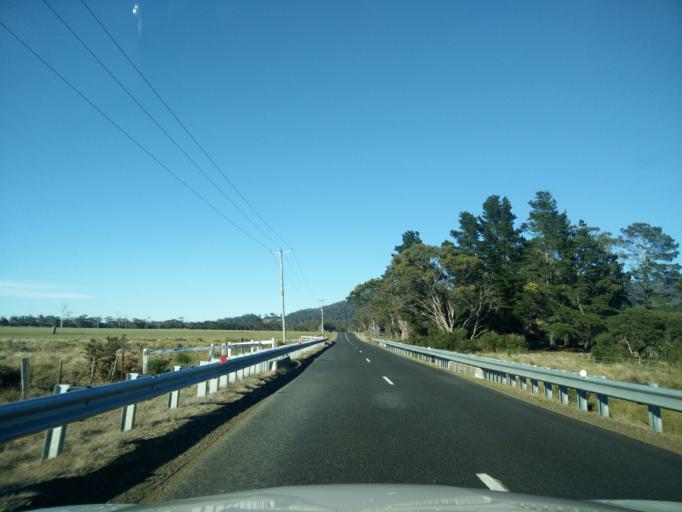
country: AU
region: Tasmania
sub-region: Break O'Day
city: St Helens
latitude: -41.8904
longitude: 148.2692
